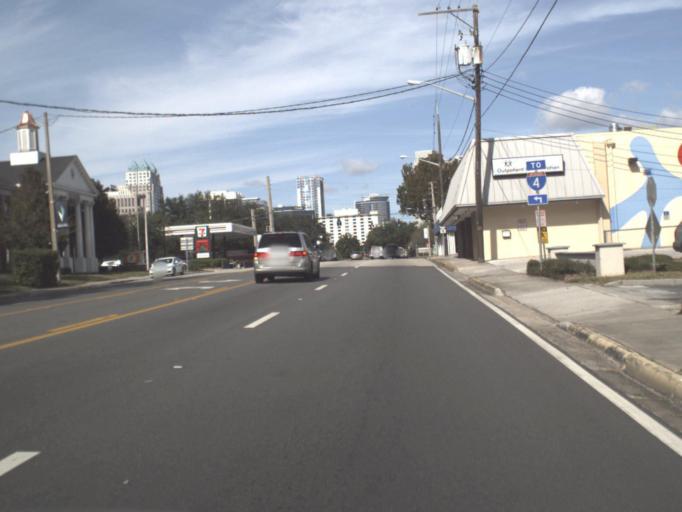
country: US
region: Florida
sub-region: Orange County
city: Orlando
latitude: 28.5297
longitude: -81.3764
